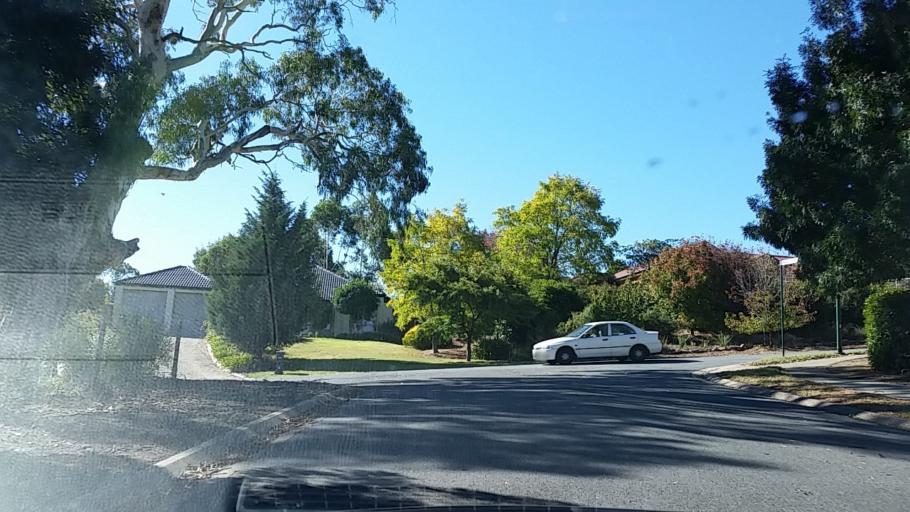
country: AU
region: South Australia
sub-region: Mount Barker
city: Mount Barker
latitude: -35.0620
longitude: 138.8769
